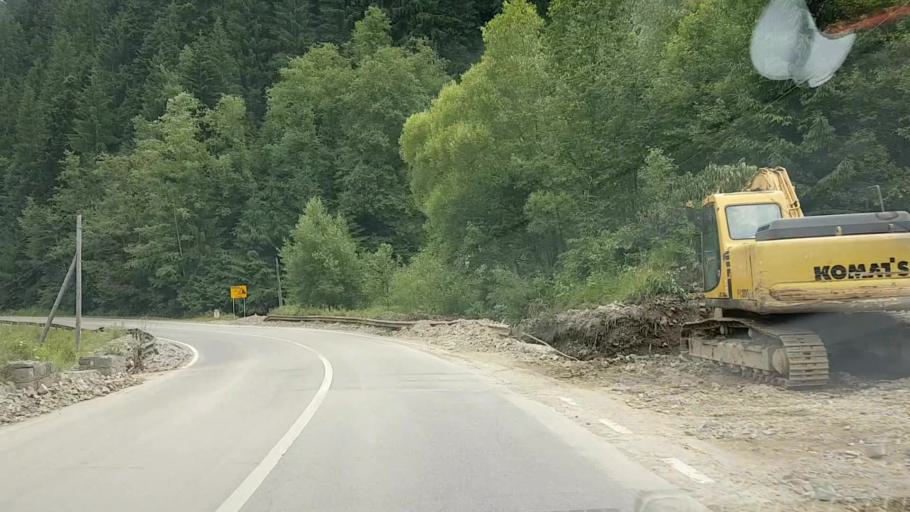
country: RO
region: Neamt
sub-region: Comuna Poiana Teiului
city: Poiana Teiului
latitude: 47.0937
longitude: 25.9460
